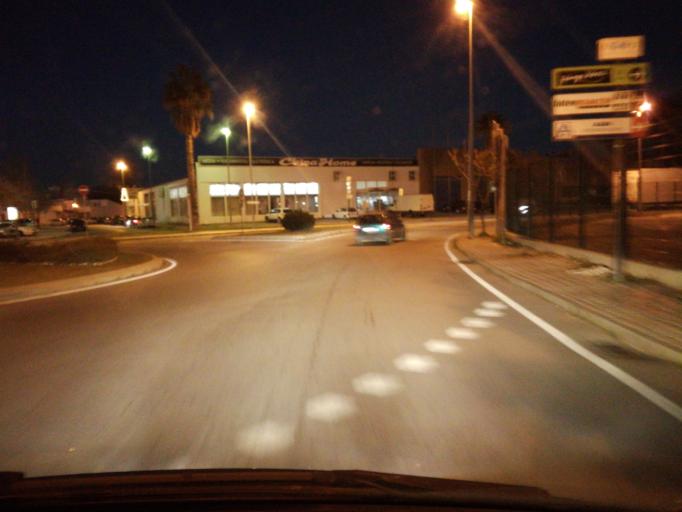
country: PT
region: Faro
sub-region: Olhao
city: Olhao
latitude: 37.0286
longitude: -7.8363
